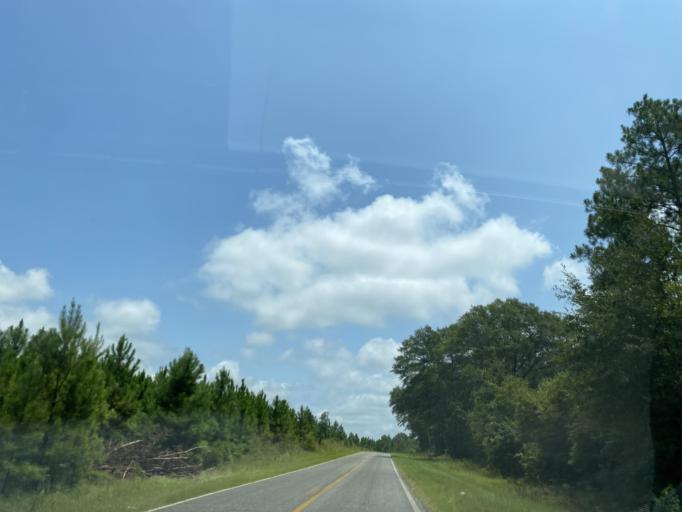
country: US
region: Georgia
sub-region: Wheeler County
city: Alamo
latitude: 32.0790
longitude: -82.7434
